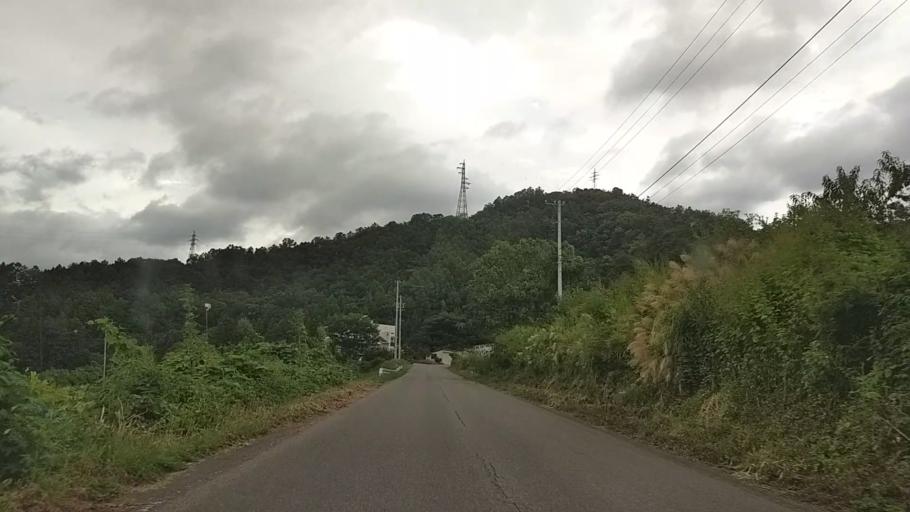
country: JP
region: Nagano
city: Iiyama
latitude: 36.8163
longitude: 138.3660
